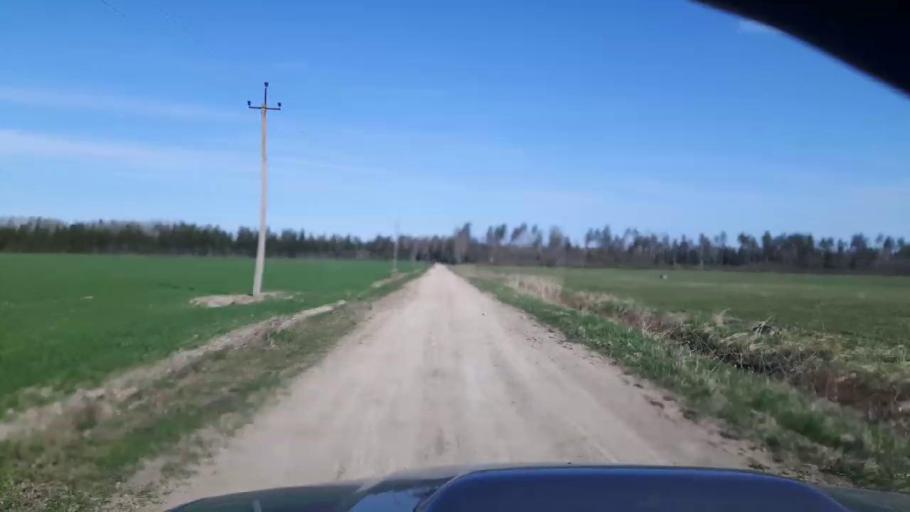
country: EE
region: Paernumaa
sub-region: Tootsi vald
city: Tootsi
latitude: 58.5117
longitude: 24.9316
